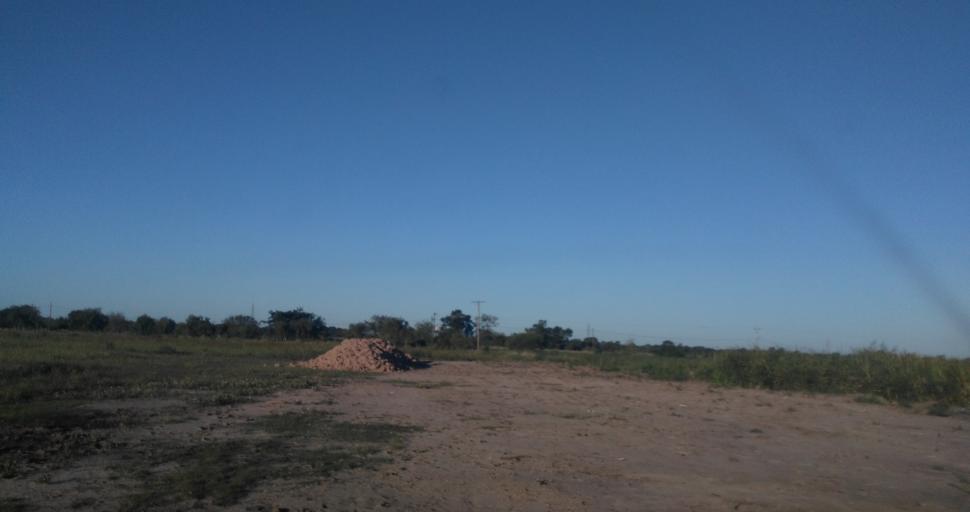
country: AR
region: Chaco
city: Fontana
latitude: -27.3936
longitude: -58.9819
